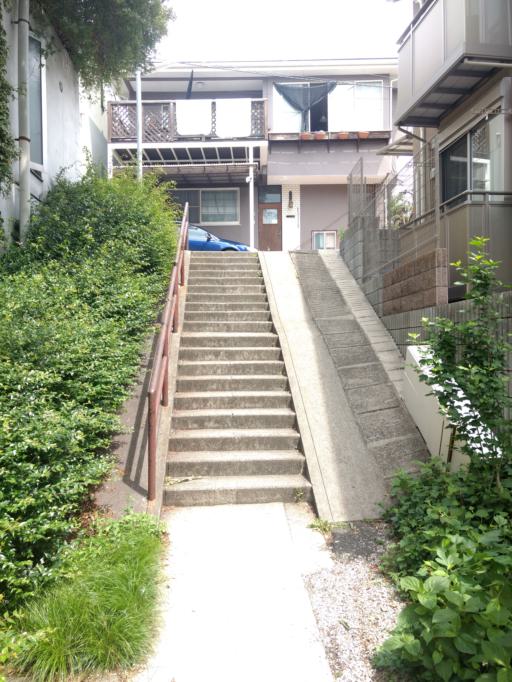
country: JP
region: Tokyo
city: Tokyo
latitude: 35.7205
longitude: 139.7009
